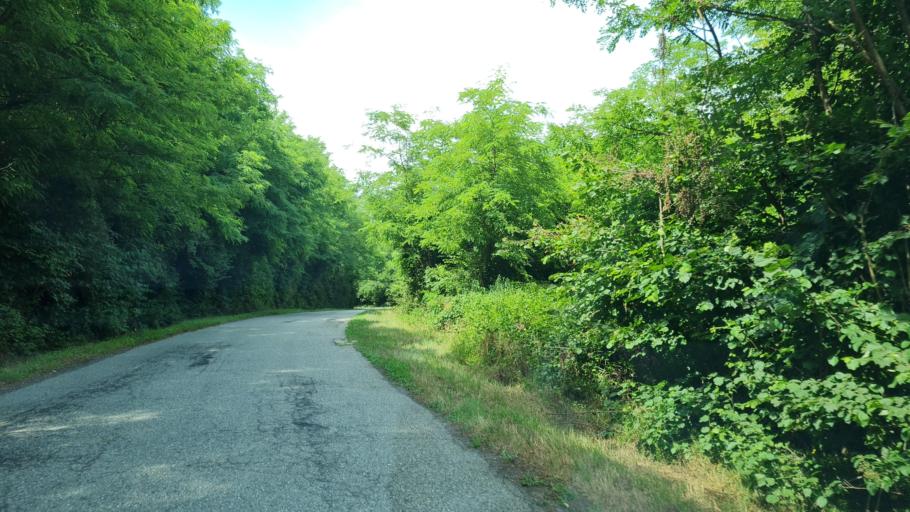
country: IT
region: Piedmont
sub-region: Provincia di Biella
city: Masserano
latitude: 45.5618
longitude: 8.2301
